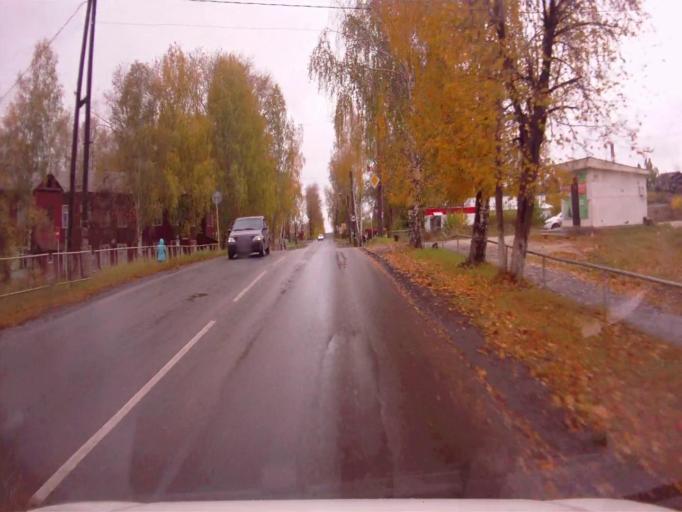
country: RU
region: Chelyabinsk
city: Verkhniy Ufaley
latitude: 56.0363
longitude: 60.2586
